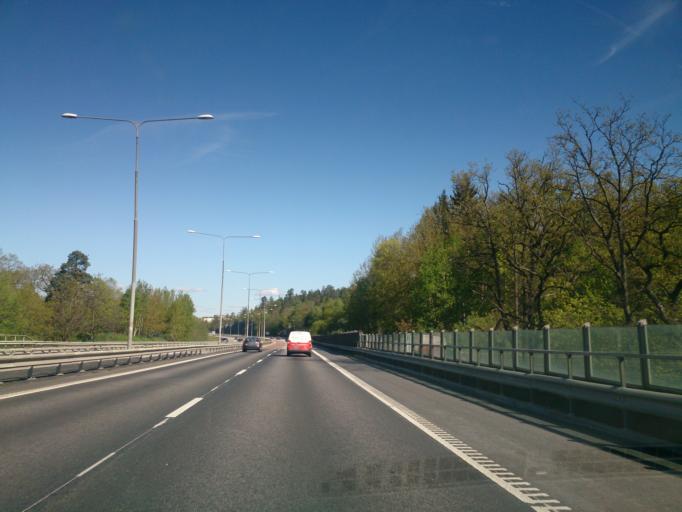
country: SE
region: Stockholm
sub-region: Haninge Kommun
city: Handen
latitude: 59.2345
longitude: 18.1232
